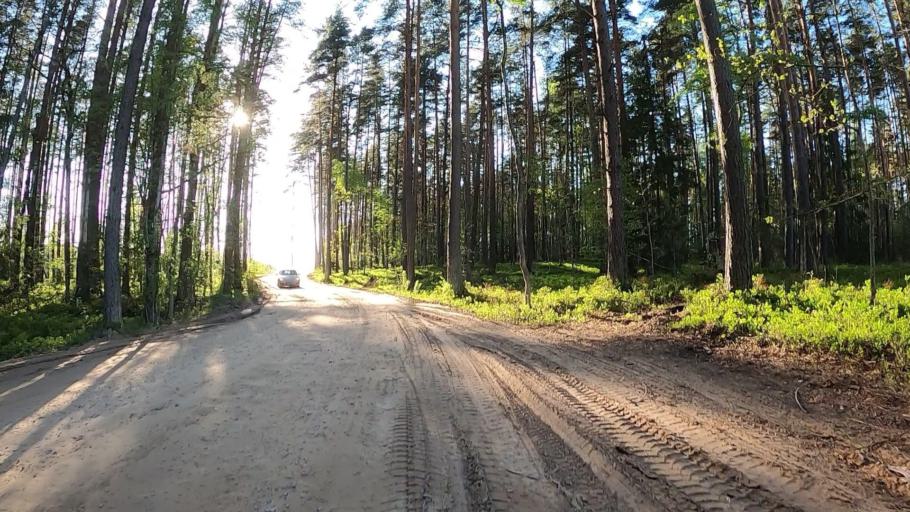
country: LV
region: Kekava
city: Kekava
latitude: 56.7819
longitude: 24.3063
